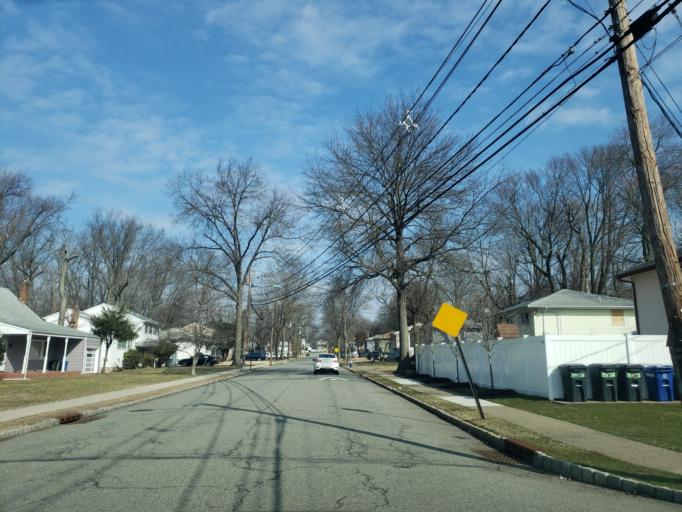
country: US
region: New Jersey
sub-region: Essex County
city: West Orange
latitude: 40.8068
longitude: -74.2572
